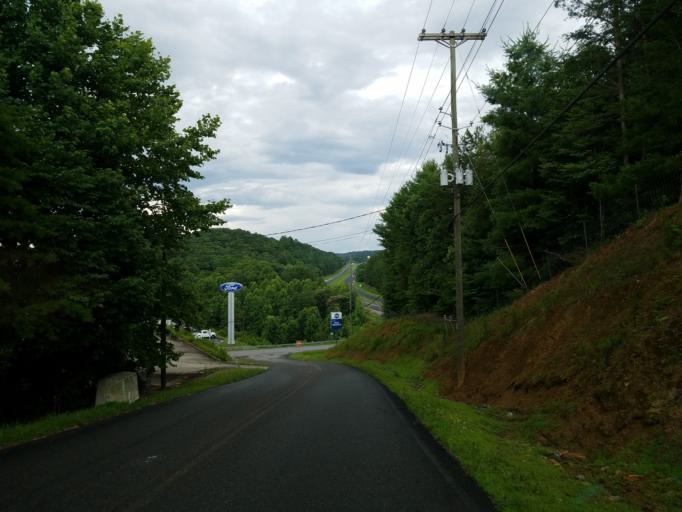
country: US
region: Georgia
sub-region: Gilmer County
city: Ellijay
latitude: 34.6687
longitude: -84.4878
